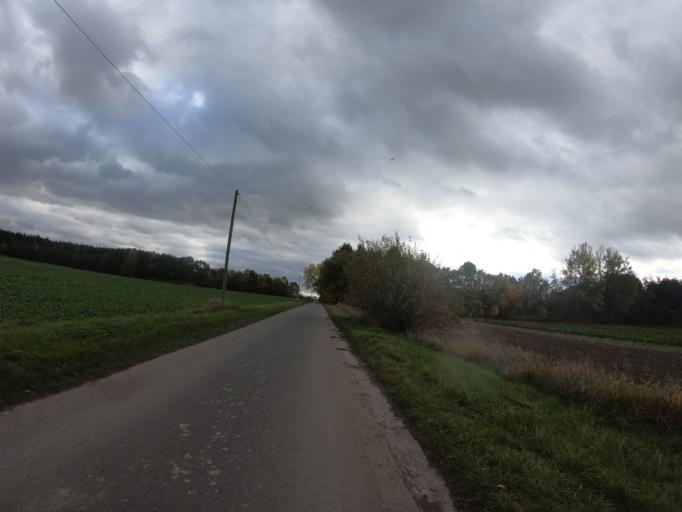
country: DE
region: Lower Saxony
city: Adenbuettel
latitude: 52.3867
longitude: 10.4852
